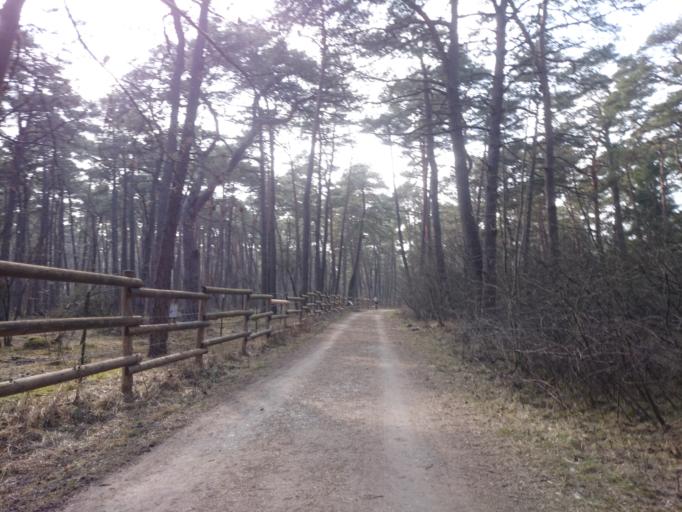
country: DE
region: Bavaria
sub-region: Swabia
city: Konigsbrunn
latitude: 48.2784
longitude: 10.9080
